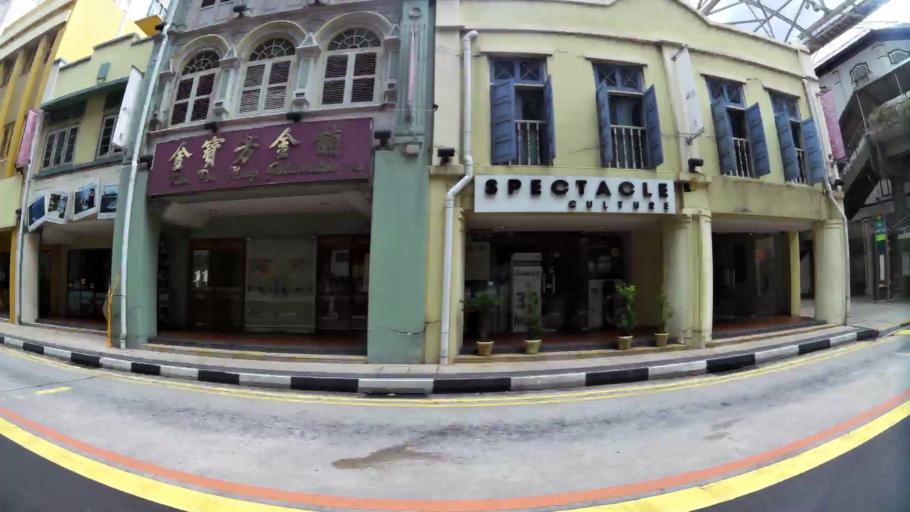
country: SG
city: Singapore
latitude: 1.2847
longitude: 103.8467
